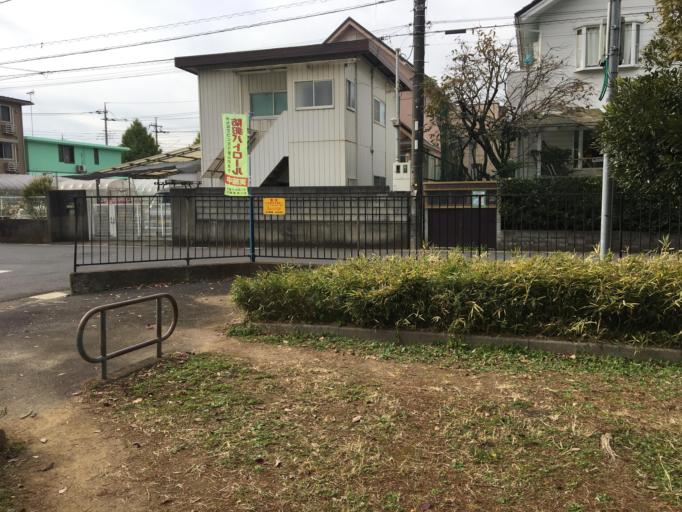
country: JP
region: Saitama
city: Yoshikawa
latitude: 35.8868
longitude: 139.8447
